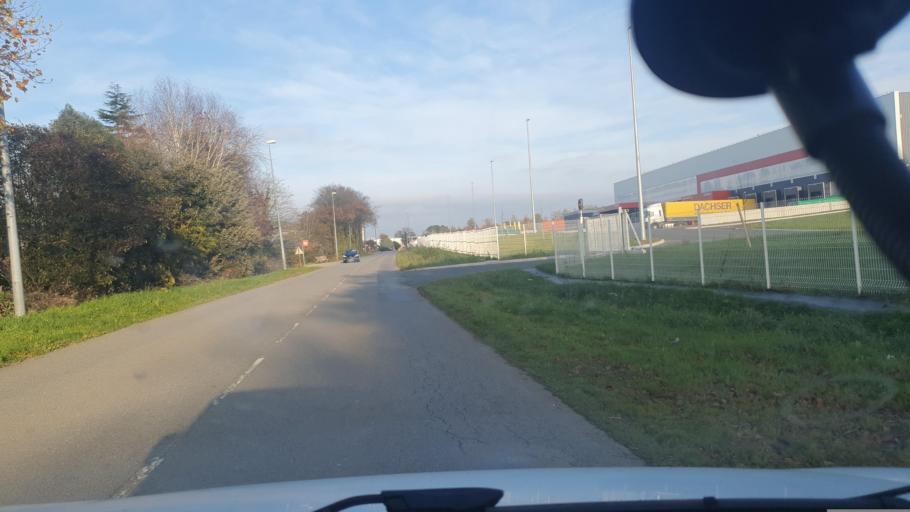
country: FR
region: Brittany
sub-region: Departement du Finistere
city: Briec
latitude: 48.0977
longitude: -4.0202
